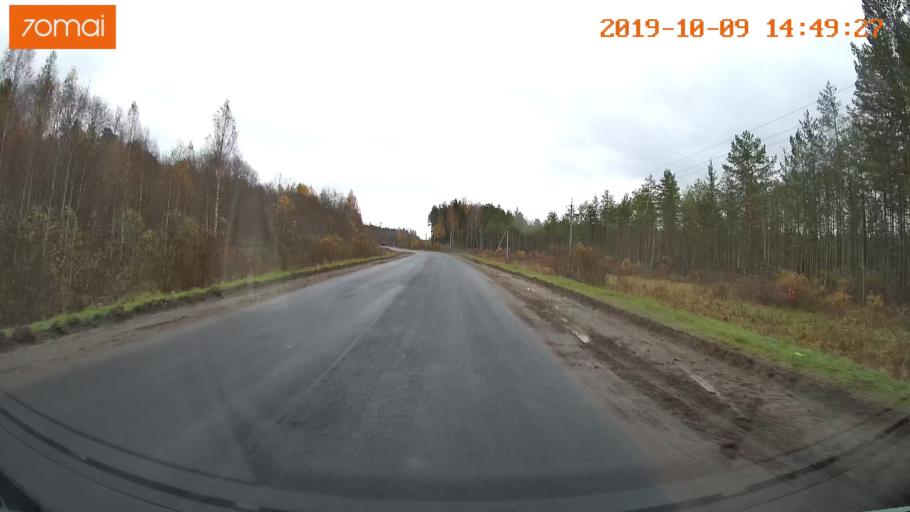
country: RU
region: Kostroma
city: Chistyye Bory
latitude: 58.3931
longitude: 41.5822
